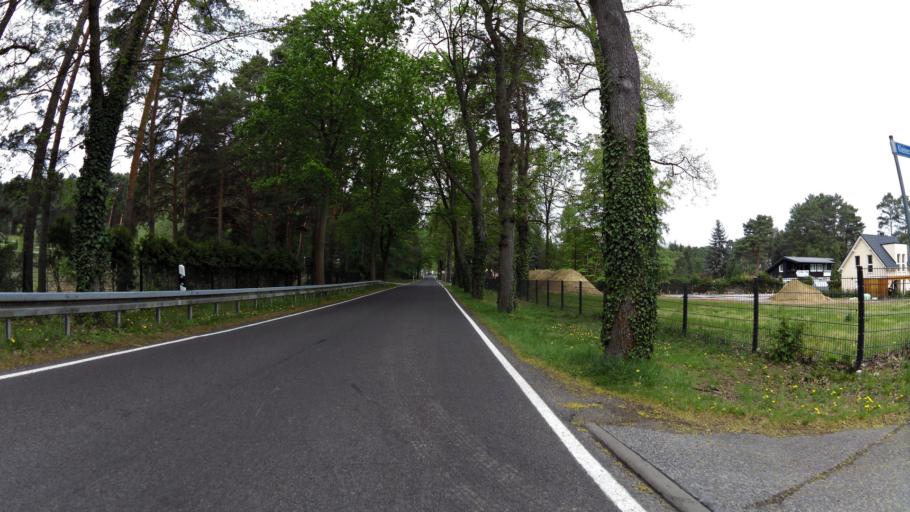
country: DE
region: Brandenburg
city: Mittenwalde
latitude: 52.2004
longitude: 13.5741
